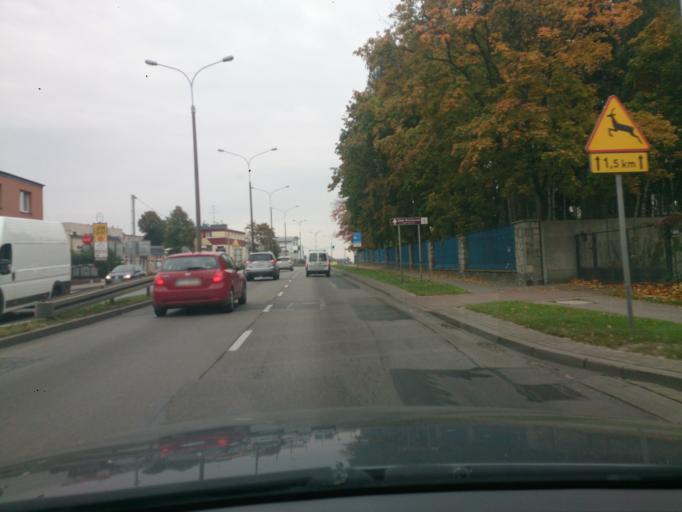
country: PL
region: Pomeranian Voivodeship
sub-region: Powiat wejherowski
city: Rumia
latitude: 54.5620
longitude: 18.3971
